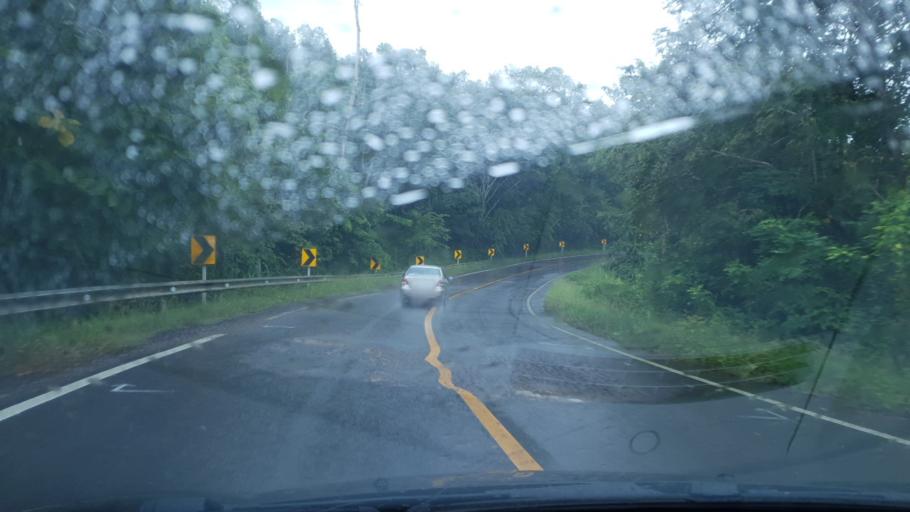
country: TH
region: Mae Hong Son
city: Khun Yuam
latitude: 18.6678
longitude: 97.9288
